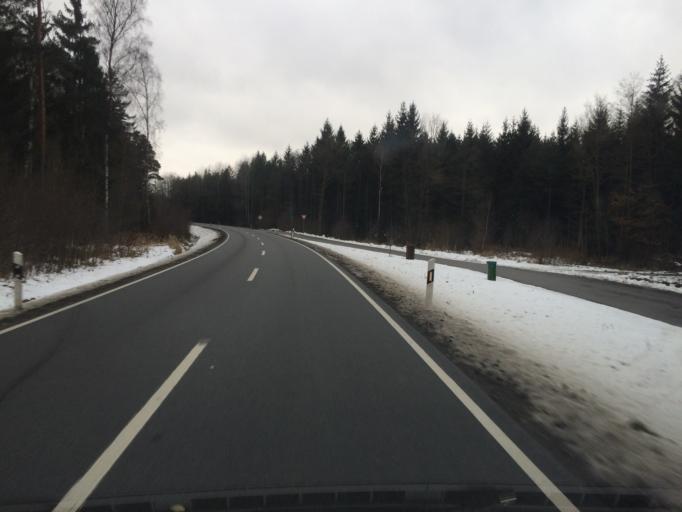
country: DE
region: Bavaria
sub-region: Upper Palatinate
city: Teublitz
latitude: 49.2211
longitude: 12.1124
